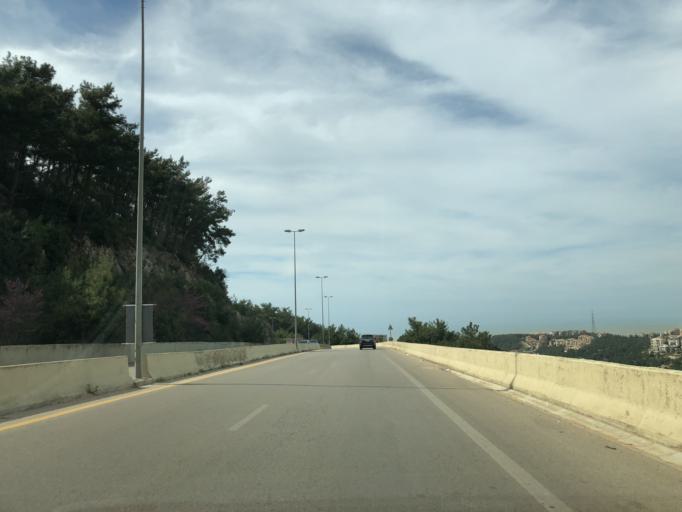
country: LB
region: Mont-Liban
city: Jdaidet el Matn
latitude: 33.9003
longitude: 35.6440
